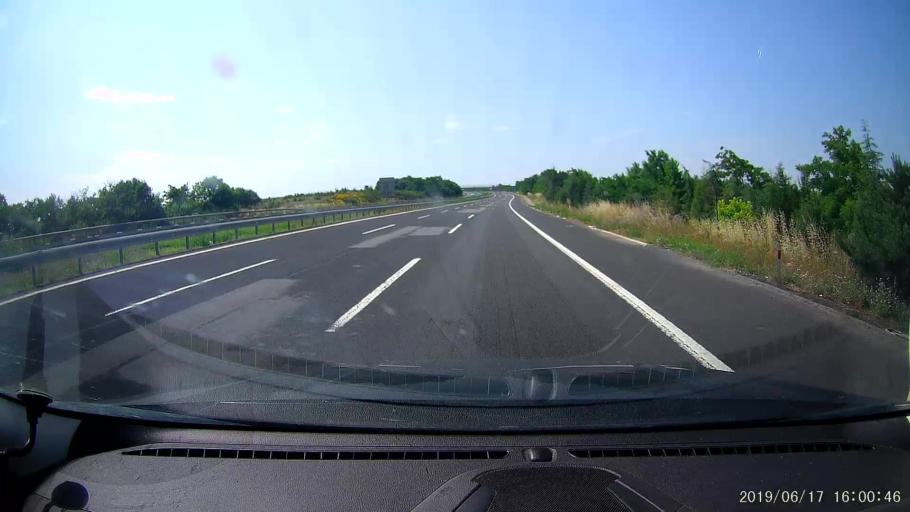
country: TR
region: Tekirdag
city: Velimese
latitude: 41.2371
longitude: 27.8619
